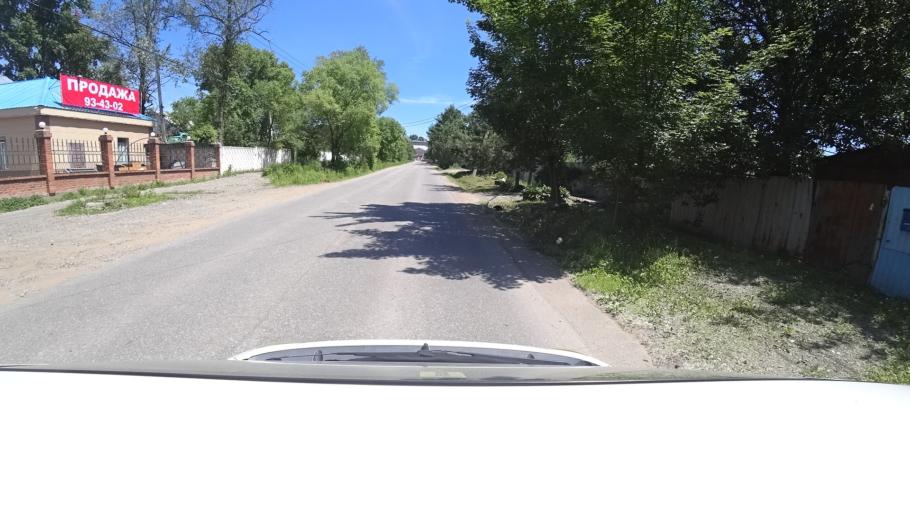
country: RU
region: Khabarovsk Krai
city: Topolevo
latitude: 48.5073
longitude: 135.1696
